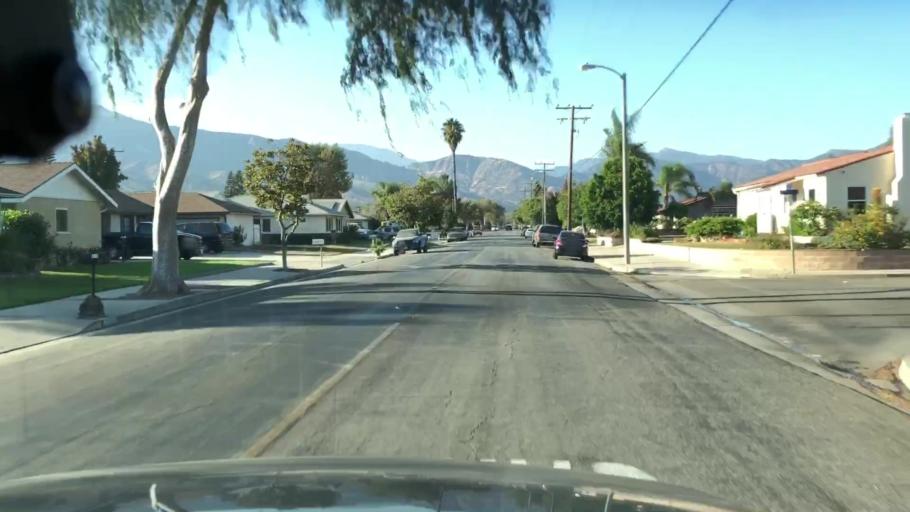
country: US
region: California
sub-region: Ventura County
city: Fillmore
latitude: 34.3967
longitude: -118.9275
